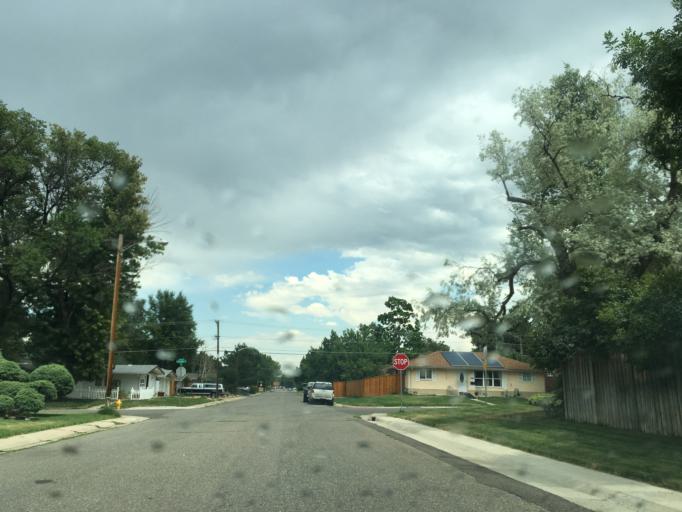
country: US
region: Colorado
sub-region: Arapahoe County
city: Sheridan
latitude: 39.6703
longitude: -105.0375
